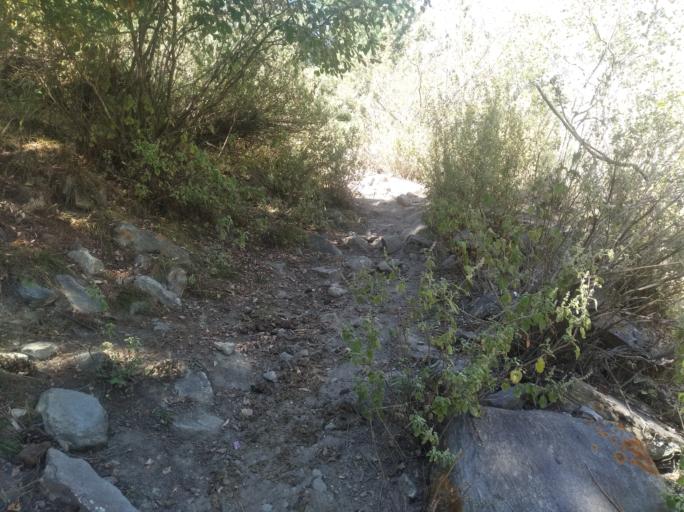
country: NP
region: Western Region
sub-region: Dhawalagiri Zone
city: Jomsom
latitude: 28.8898
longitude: 83.0740
